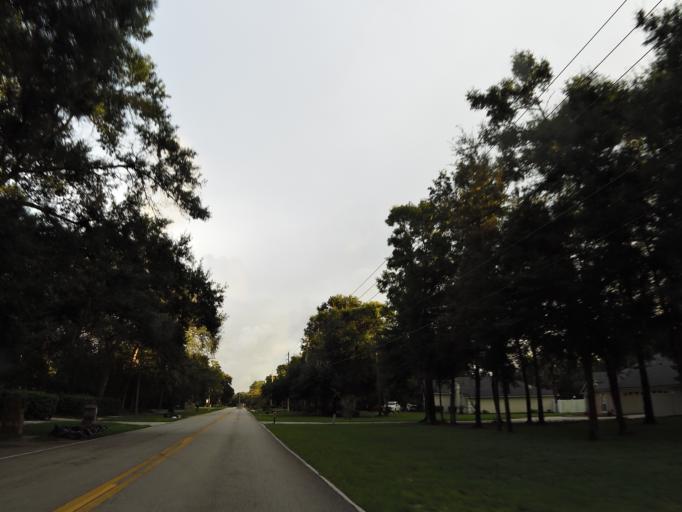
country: US
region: Florida
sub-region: Duval County
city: Atlantic Beach
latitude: 30.3656
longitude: -81.4844
